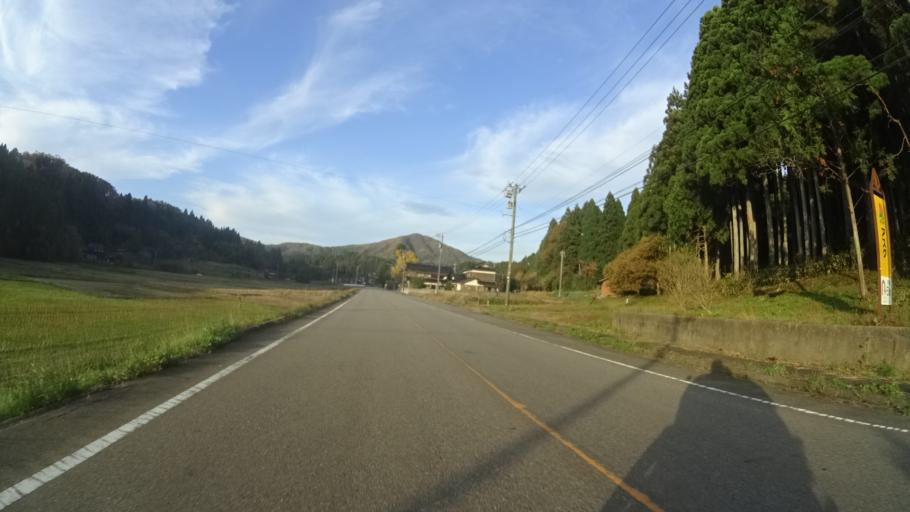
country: JP
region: Ishikawa
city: Nanao
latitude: 37.1880
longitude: 136.7159
